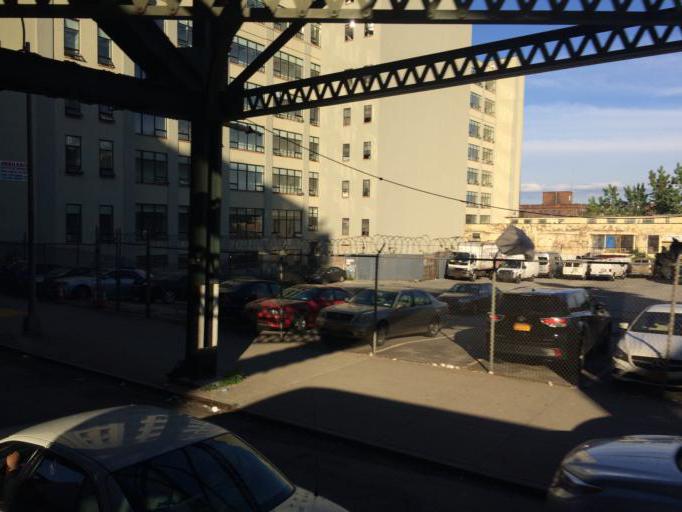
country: US
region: New York
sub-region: Queens County
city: Long Island City
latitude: 40.7511
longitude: -73.9346
